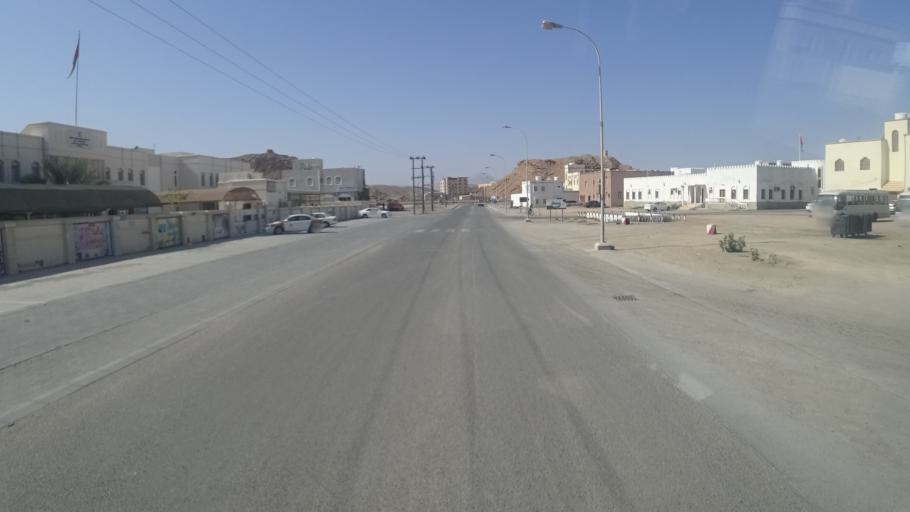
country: OM
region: Ash Sharqiyah
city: Sur
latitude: 22.5655
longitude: 59.5446
